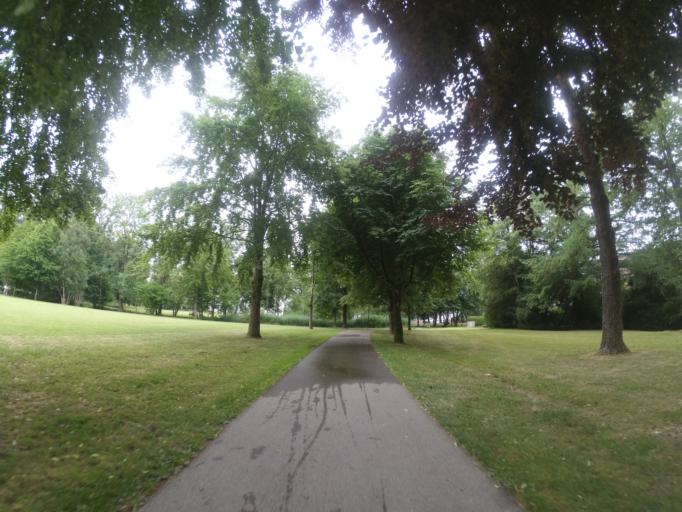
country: DE
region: Baden-Wuerttemberg
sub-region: Tuebingen Region
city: Kisslegg
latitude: 47.7905
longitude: 9.8816
